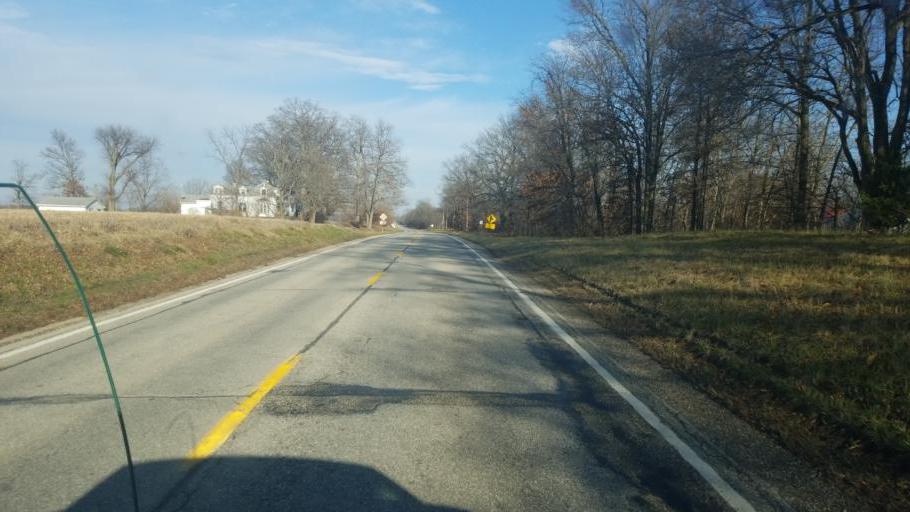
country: US
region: Illinois
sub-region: Wabash County
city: Mount Carmel
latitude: 38.3508
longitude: -87.8701
